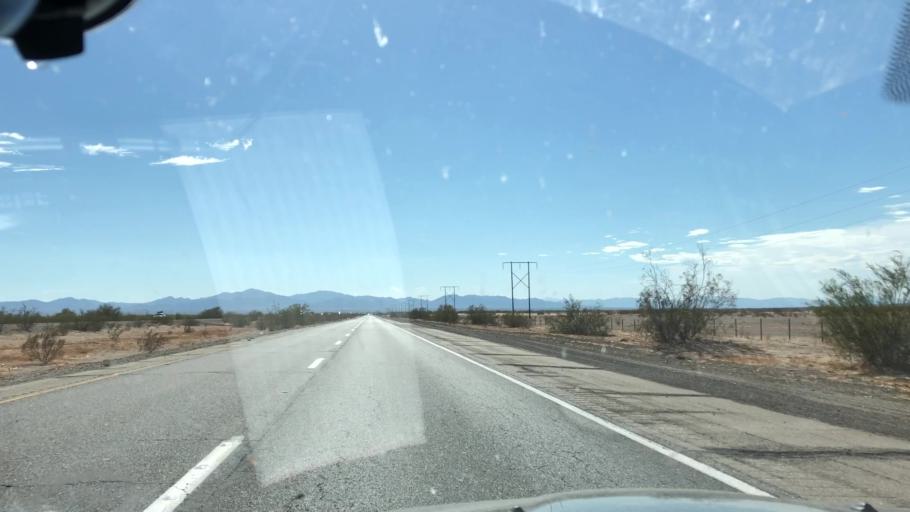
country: US
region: California
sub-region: Riverside County
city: Mesa Verde
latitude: 33.6062
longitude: -114.9485
